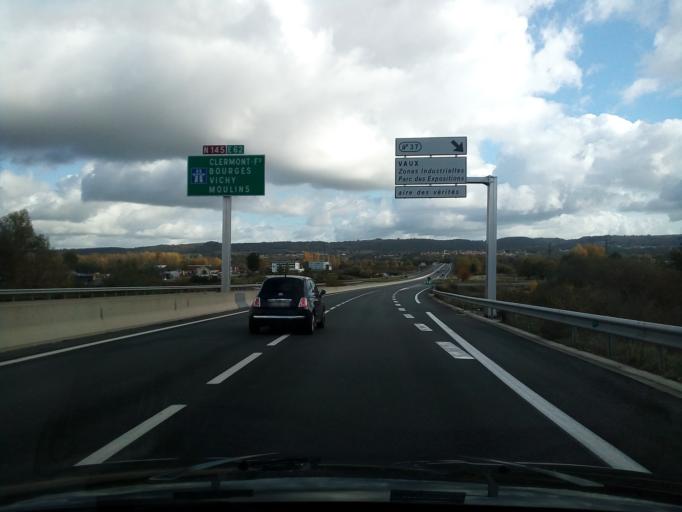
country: FR
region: Auvergne
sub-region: Departement de l'Allier
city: Saint-Victor
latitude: 46.3760
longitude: 2.5812
